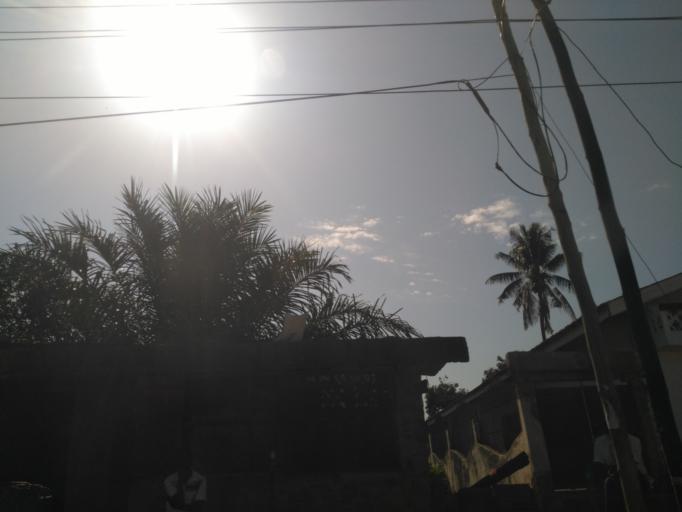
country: TZ
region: Mwanza
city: Mwanza
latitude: -2.5056
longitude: 32.8986
